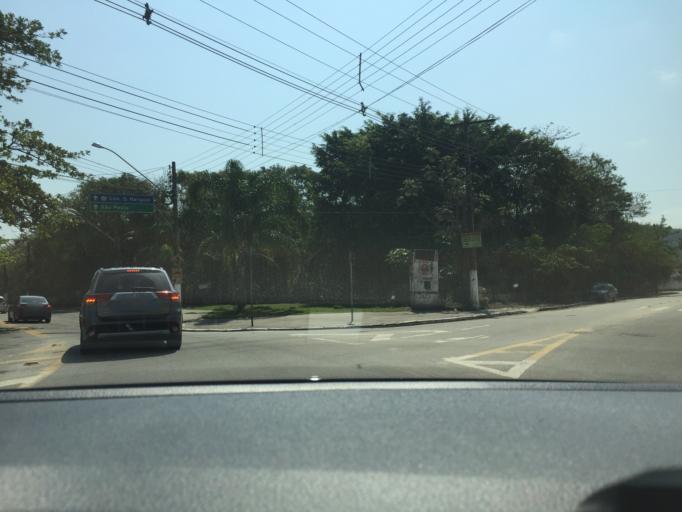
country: BR
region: Sao Paulo
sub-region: Guaruja
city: Guaruja
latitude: -23.9792
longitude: -46.2093
